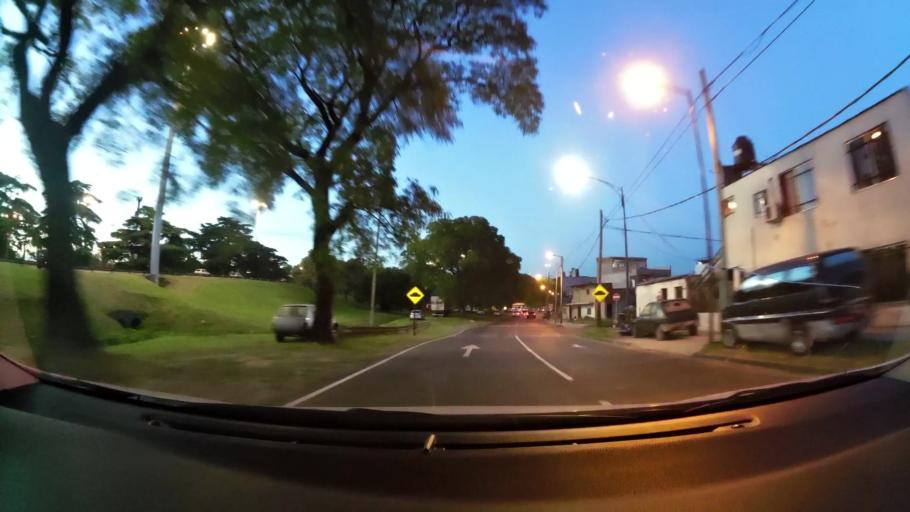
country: AR
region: Buenos Aires F.D.
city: Villa Lugano
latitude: -34.6883
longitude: -58.4824
